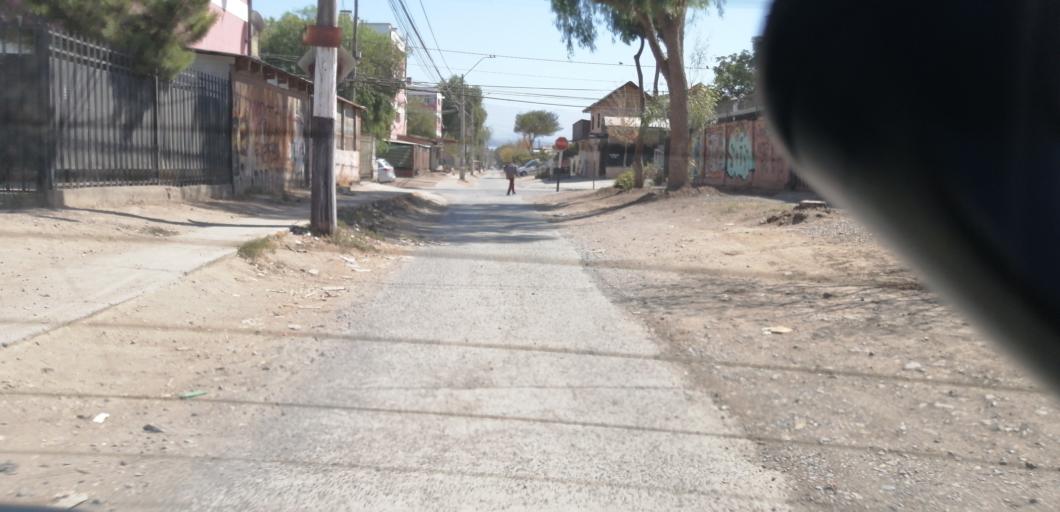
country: CL
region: Santiago Metropolitan
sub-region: Provincia de Santiago
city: Lo Prado
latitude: -33.4508
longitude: -70.7446
